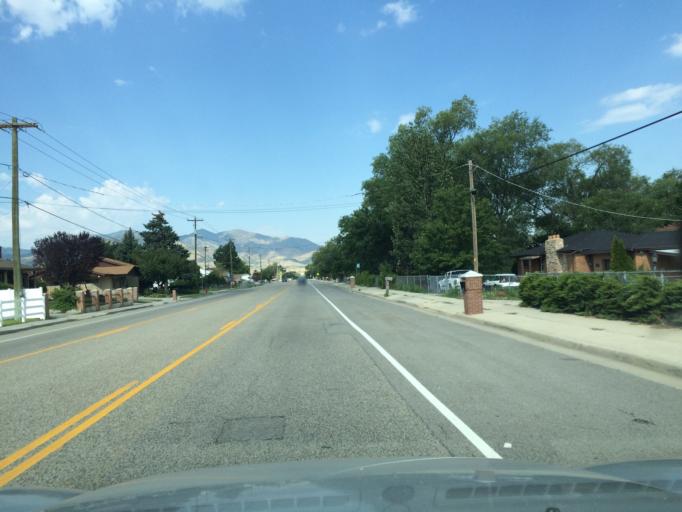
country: US
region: Utah
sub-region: Salt Lake County
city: West Valley City
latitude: 40.6966
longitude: -112.0385
